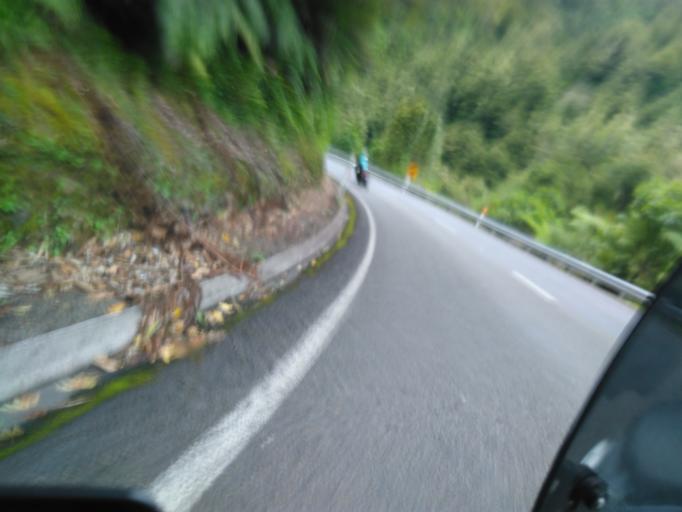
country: NZ
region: Bay of Plenty
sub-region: Opotiki District
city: Opotiki
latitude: -38.2713
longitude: 177.3202
